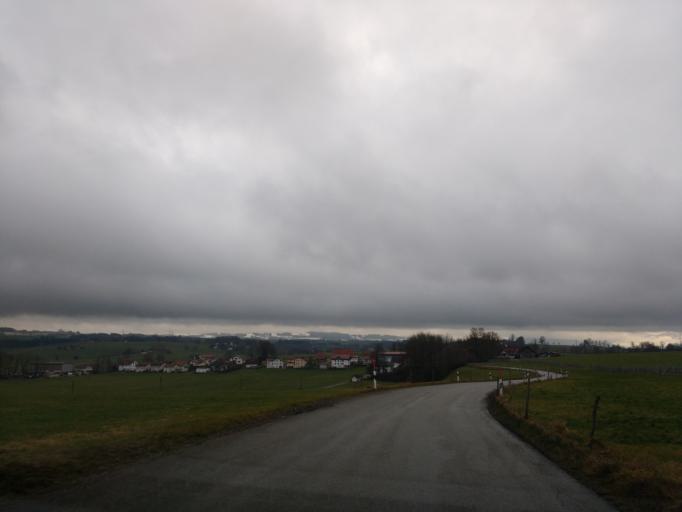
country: DE
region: Bavaria
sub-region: Swabia
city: Neuburg
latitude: 47.7412
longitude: 10.3525
